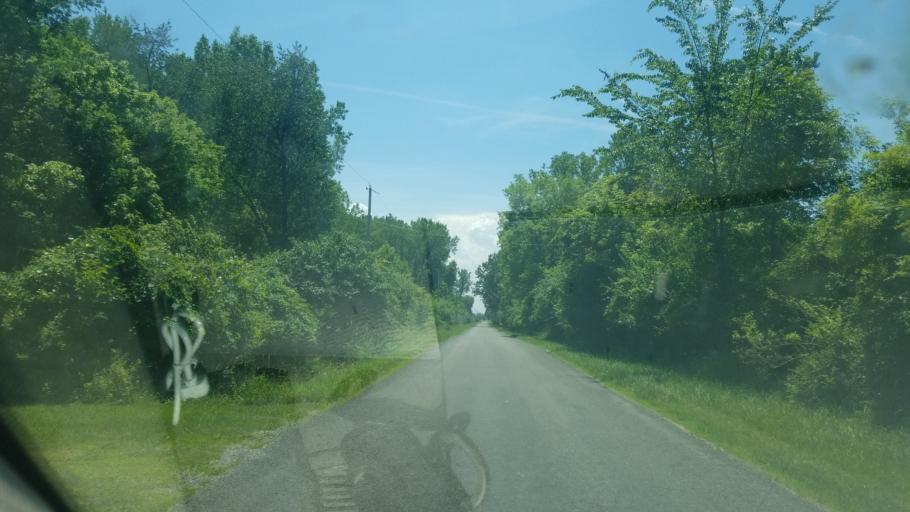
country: US
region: Ohio
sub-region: Hancock County
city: Findlay
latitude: 41.0044
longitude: -83.6363
